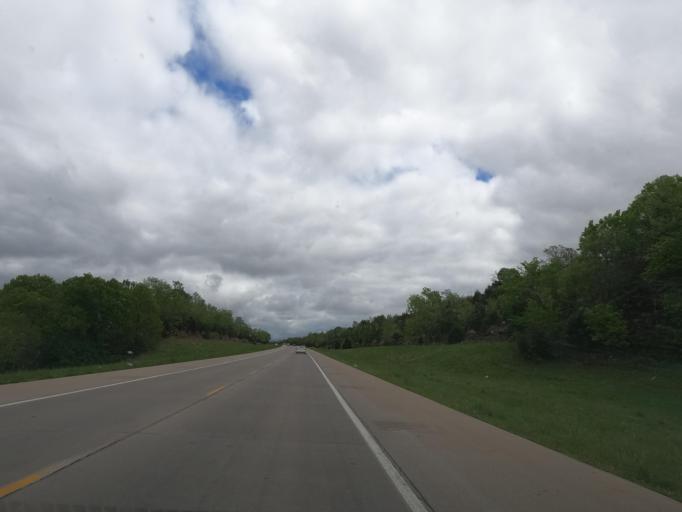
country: US
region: Kansas
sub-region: Wilson County
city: Neodesha
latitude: 37.3557
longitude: -95.6725
